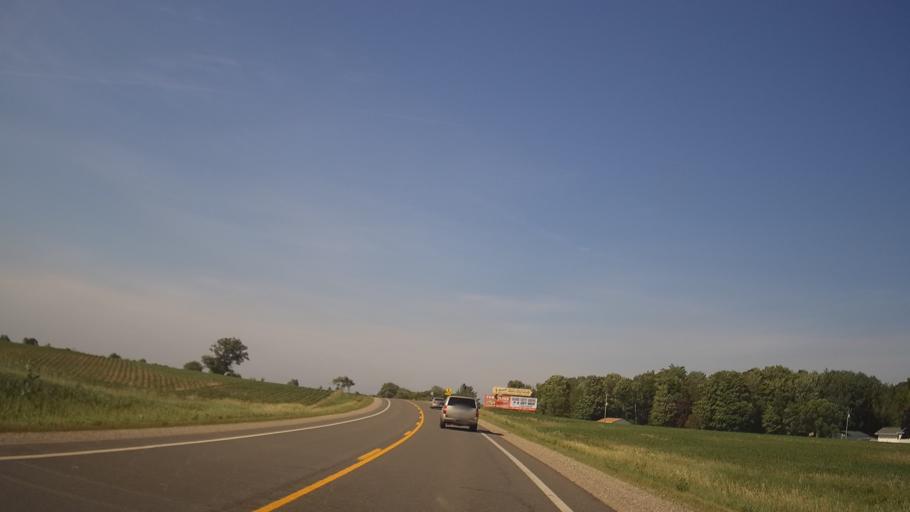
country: US
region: Michigan
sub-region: Ogemaw County
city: West Branch
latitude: 44.3671
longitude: -84.1180
